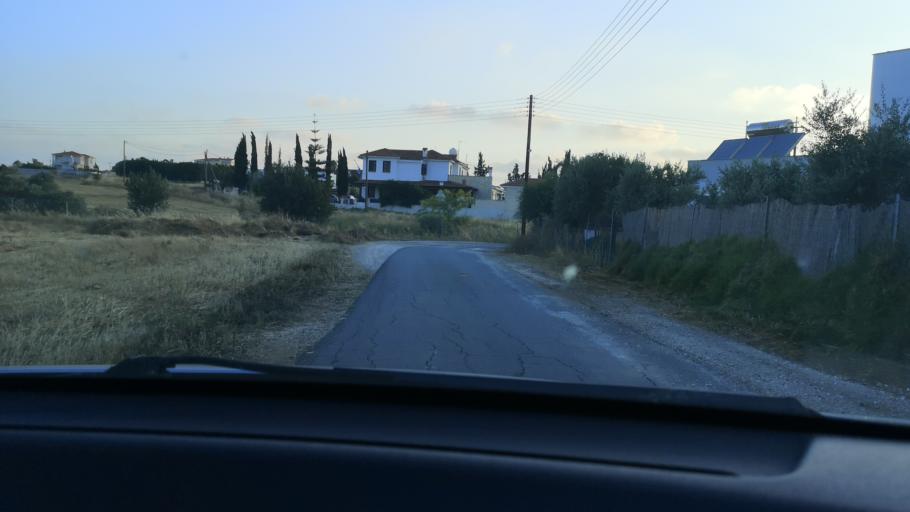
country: CY
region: Lefkosia
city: Kokkinotrimithia
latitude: 35.1201
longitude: 33.2344
